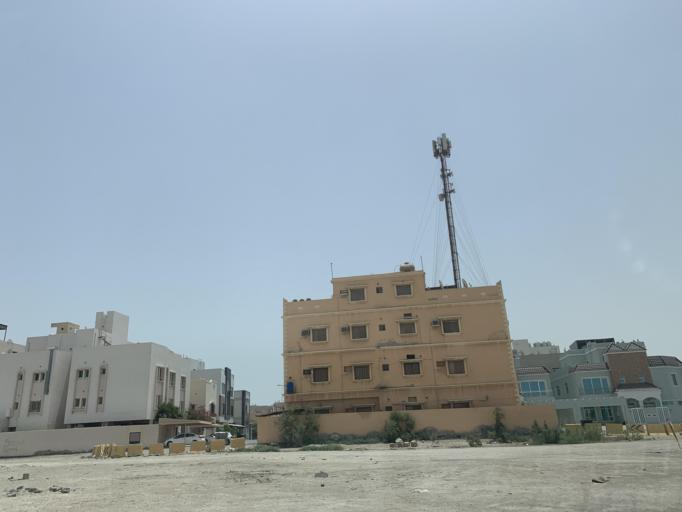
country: BH
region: Northern
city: Sitrah
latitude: 26.1435
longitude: 50.5903
